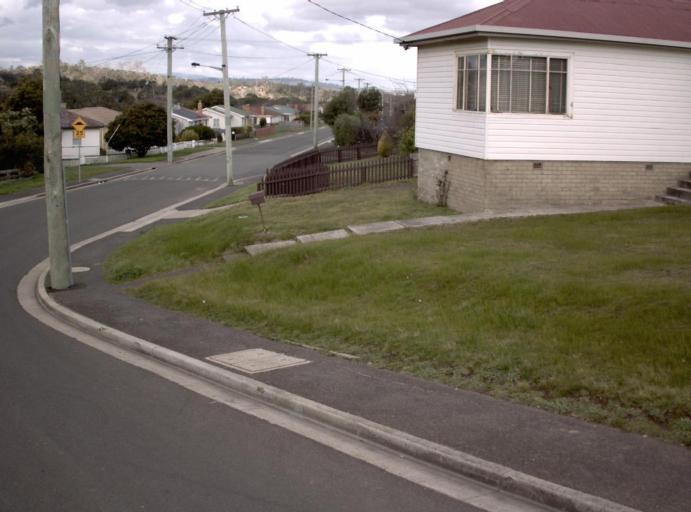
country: AU
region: Tasmania
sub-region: Launceston
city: Mayfield
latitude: -41.3858
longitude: 147.1335
